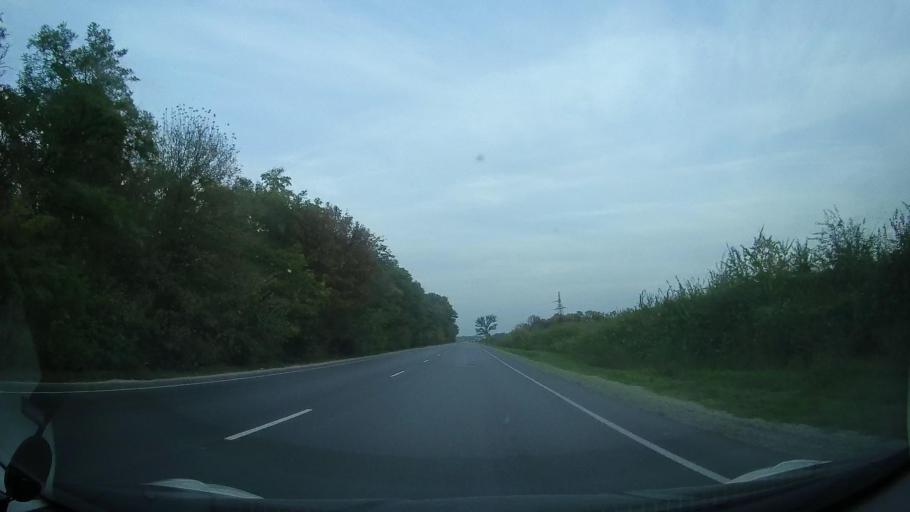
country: RU
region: Rostov
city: Ol'ginskaya
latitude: 47.1313
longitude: 39.9504
